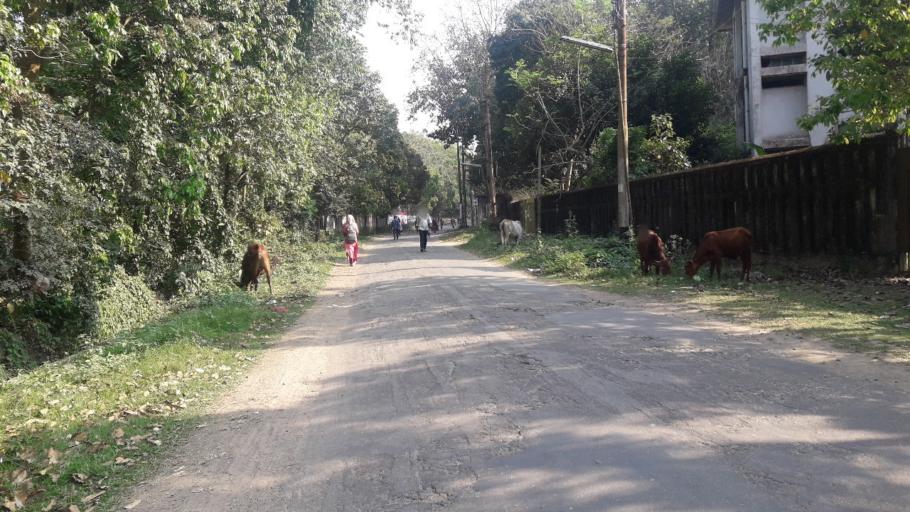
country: BD
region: Chittagong
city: Chittagong
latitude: 22.4687
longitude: 91.7880
